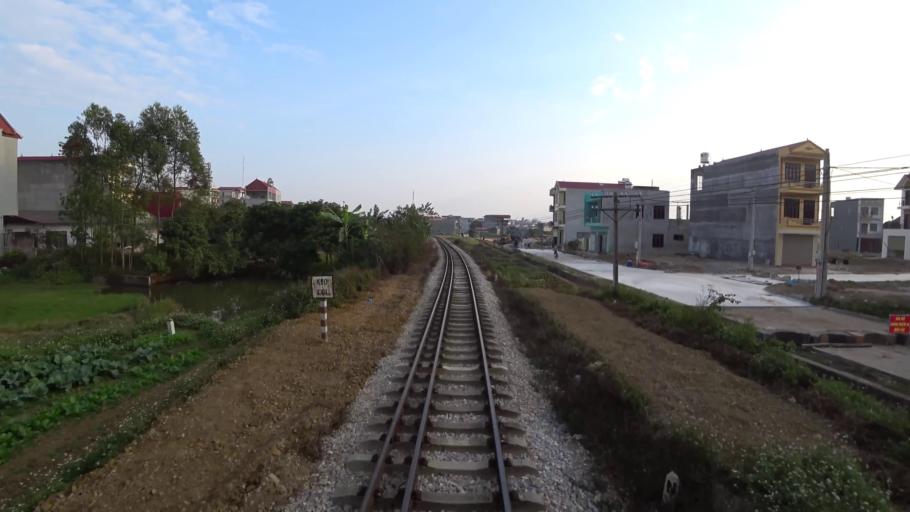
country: VN
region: Lang Son
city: Thi Tran Cao Loc
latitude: 21.8801
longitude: 106.7497
